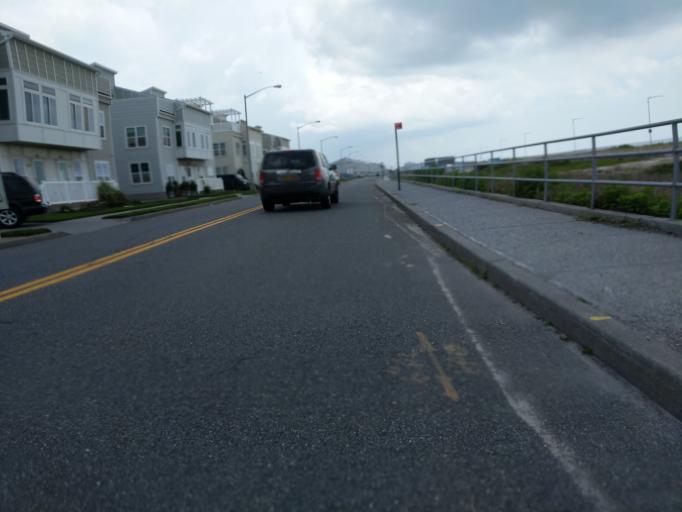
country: US
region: New York
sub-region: Nassau County
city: Inwood
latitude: 40.5870
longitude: -73.7996
